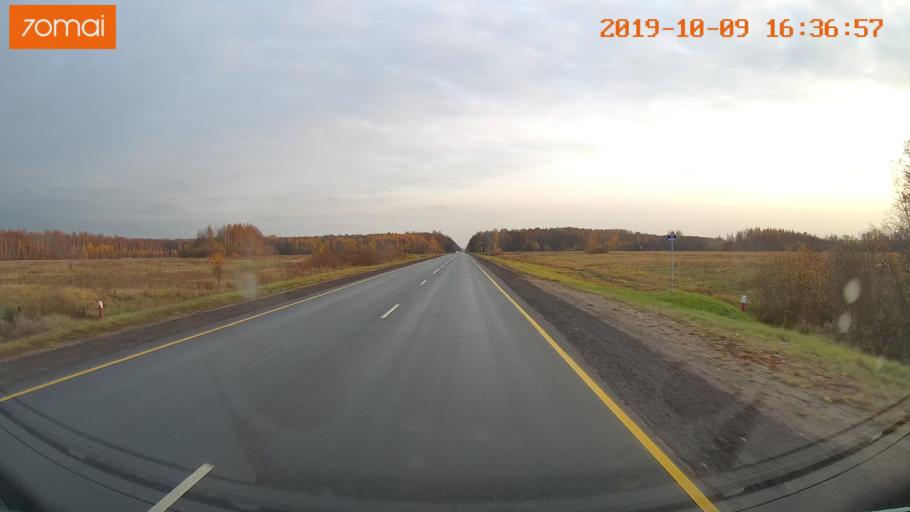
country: RU
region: Kostroma
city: Volgorechensk
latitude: 57.5342
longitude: 41.0187
